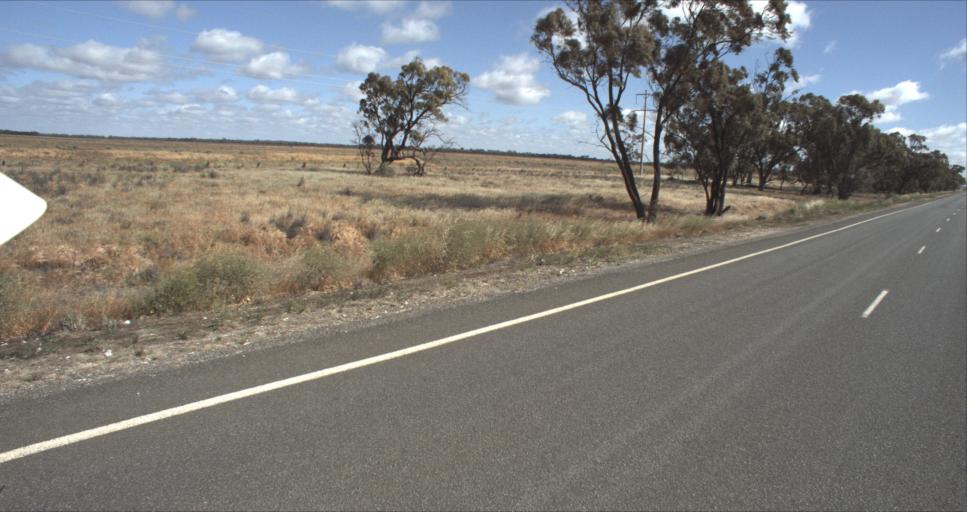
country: AU
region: New South Wales
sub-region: Murrumbidgee Shire
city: Darlington Point
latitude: -34.5608
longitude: 146.1691
